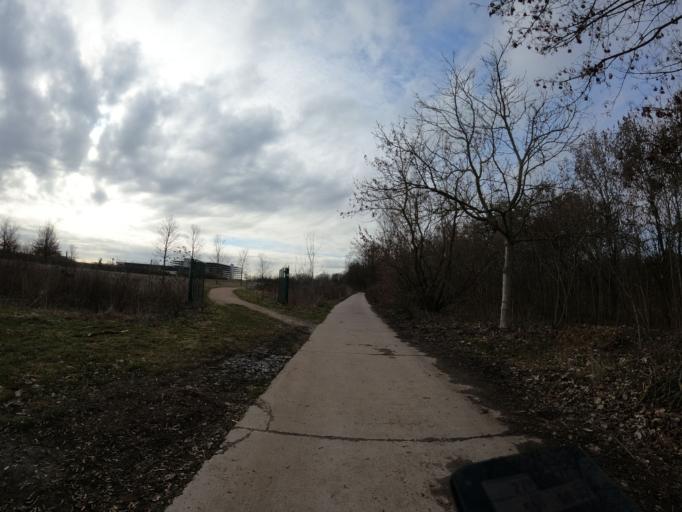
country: DE
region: Berlin
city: Altglienicke
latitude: 52.3932
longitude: 13.5331
